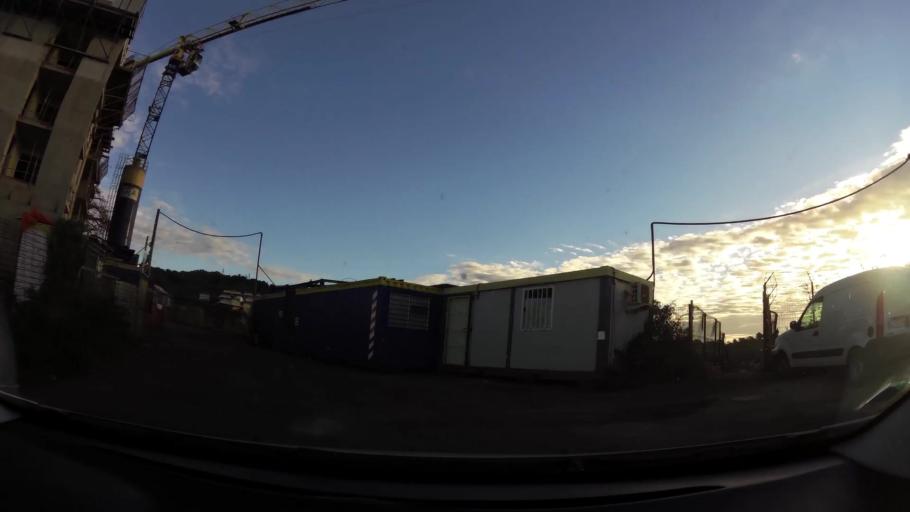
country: YT
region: Koungou
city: Koungou
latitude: -12.7349
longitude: 45.2033
